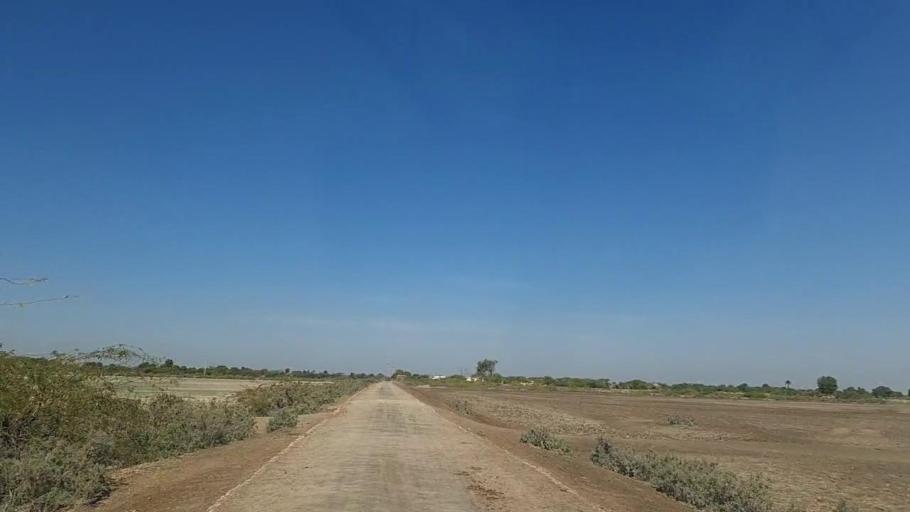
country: PK
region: Sindh
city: Samaro
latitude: 25.3055
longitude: 69.4858
